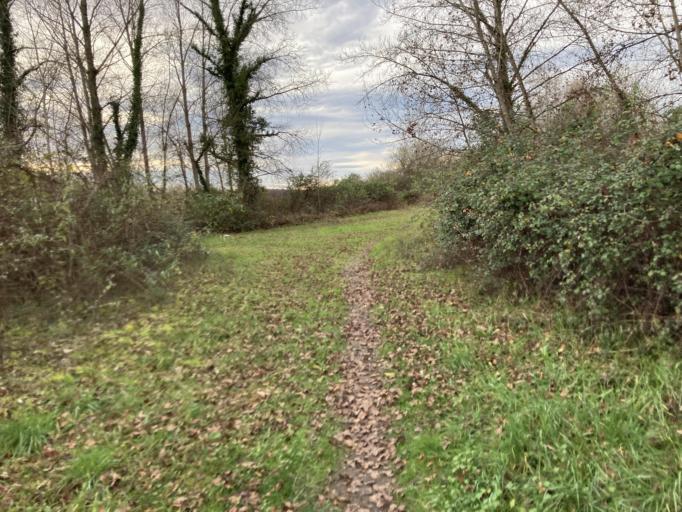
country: FR
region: Aquitaine
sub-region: Departement des Pyrenees-Atlantiques
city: Artiguelouve
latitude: 43.3324
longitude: -0.4652
